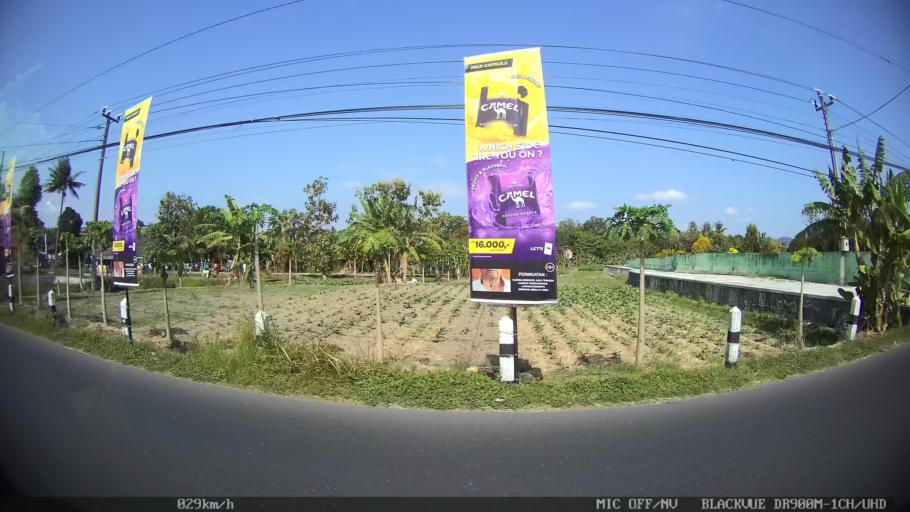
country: ID
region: Daerah Istimewa Yogyakarta
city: Sewon
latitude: -7.8762
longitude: 110.3914
